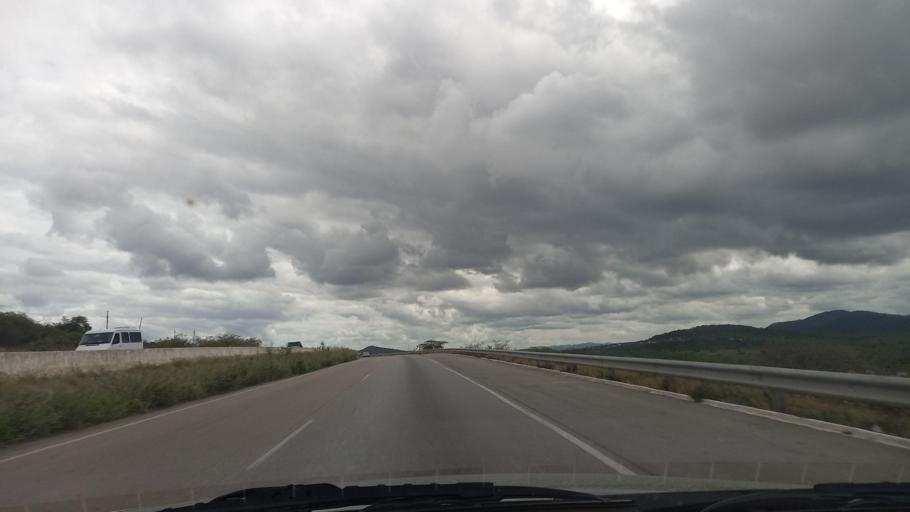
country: BR
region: Pernambuco
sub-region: Caruaru
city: Caruaru
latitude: -8.3238
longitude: -36.1081
